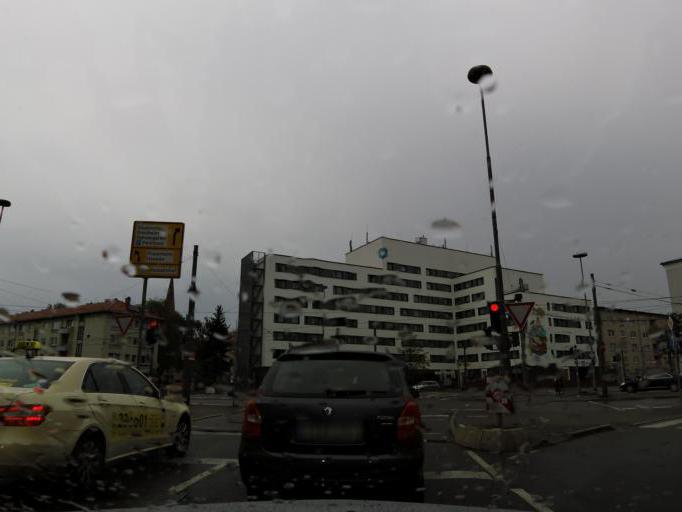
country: DE
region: Hesse
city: Niederrad
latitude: 50.1187
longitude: 8.6435
